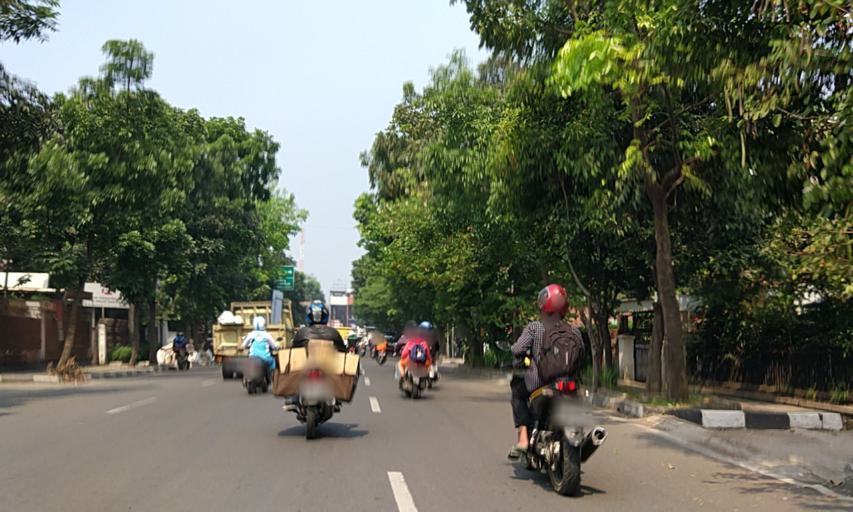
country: ID
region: West Java
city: Bandung
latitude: -6.9157
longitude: 107.5771
